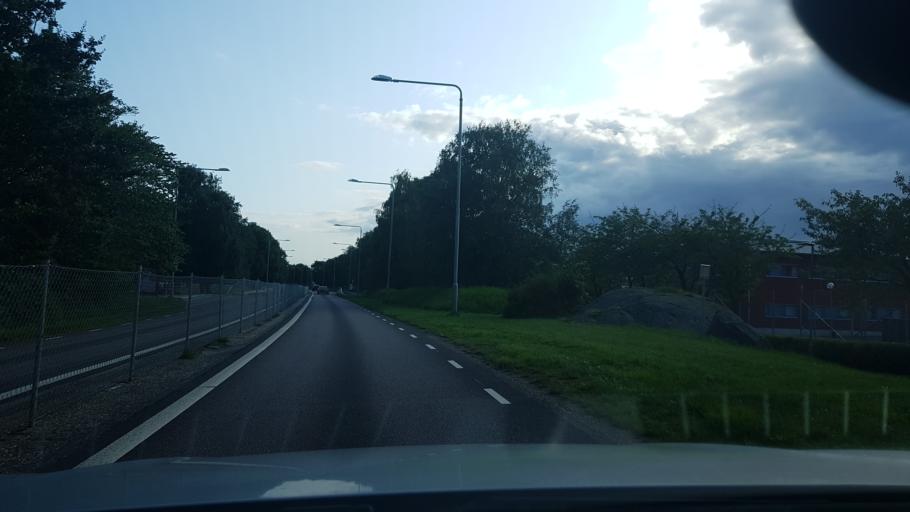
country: SE
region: Vaestra Goetaland
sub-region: Goteborg
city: Majorna
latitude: 57.6533
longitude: 11.8695
